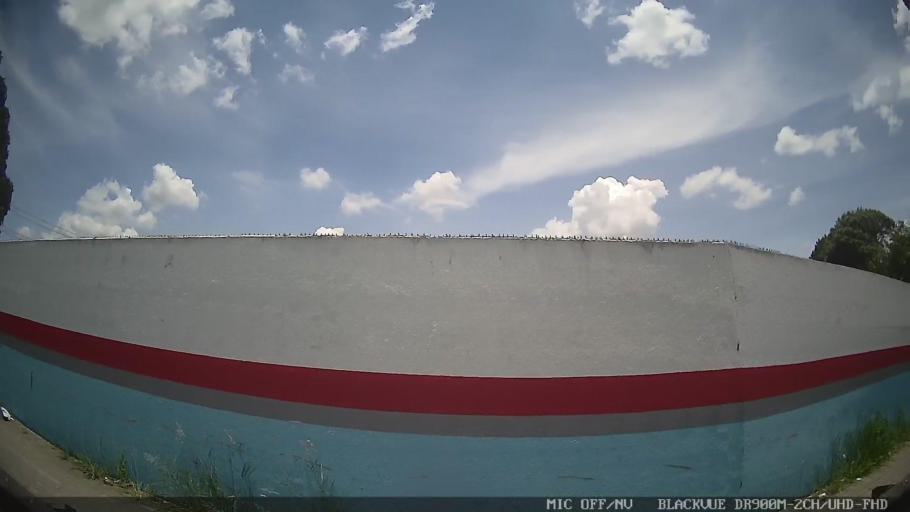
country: BR
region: Sao Paulo
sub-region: Suzano
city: Suzano
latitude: -23.5376
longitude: -46.3035
